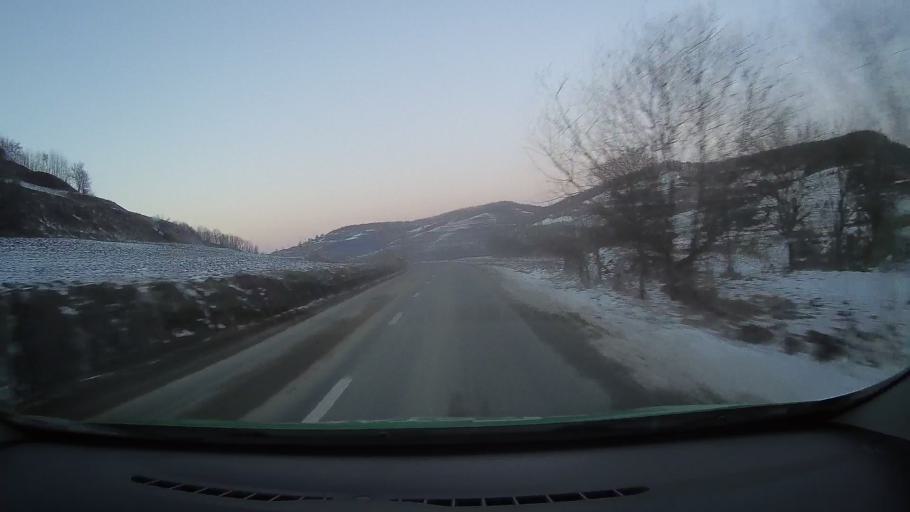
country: RO
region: Sibiu
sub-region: Comuna Atel
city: Atel
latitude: 46.1716
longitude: 24.4694
